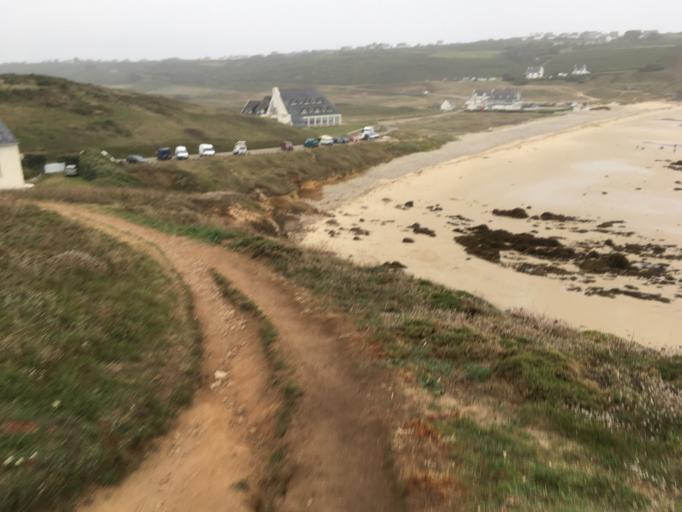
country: FR
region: Brittany
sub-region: Departement du Finistere
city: Plogoff
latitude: 48.0498
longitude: -4.7060
